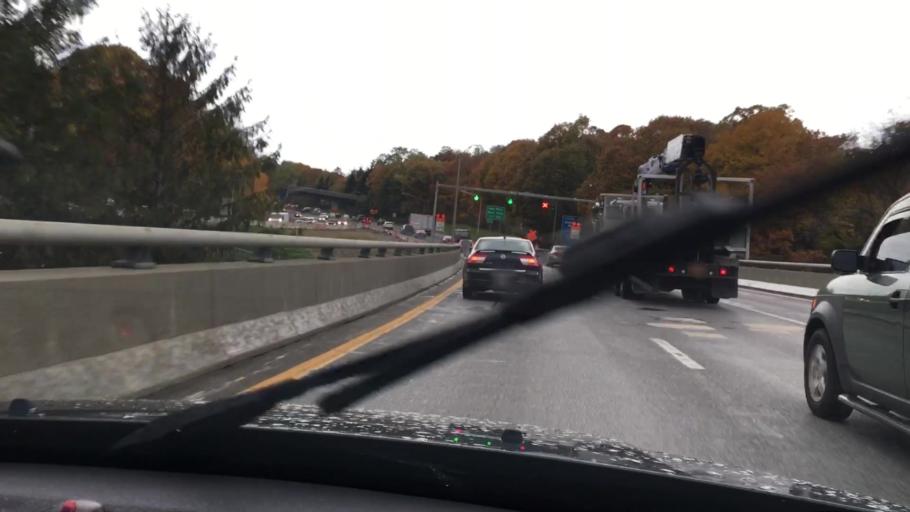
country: US
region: New York
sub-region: Orange County
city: Balmville
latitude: 41.5212
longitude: -74.0096
